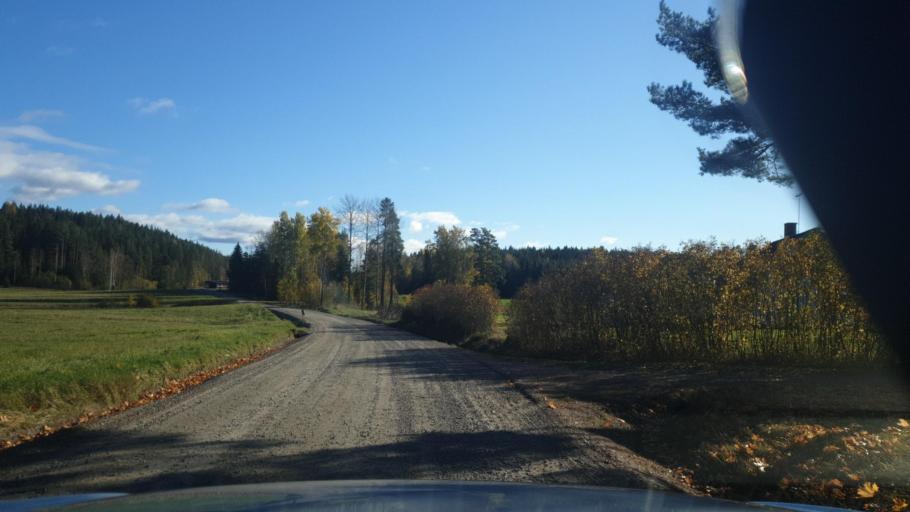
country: SE
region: Vaermland
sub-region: Arvika Kommun
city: Arvika
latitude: 59.6206
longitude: 12.8925
